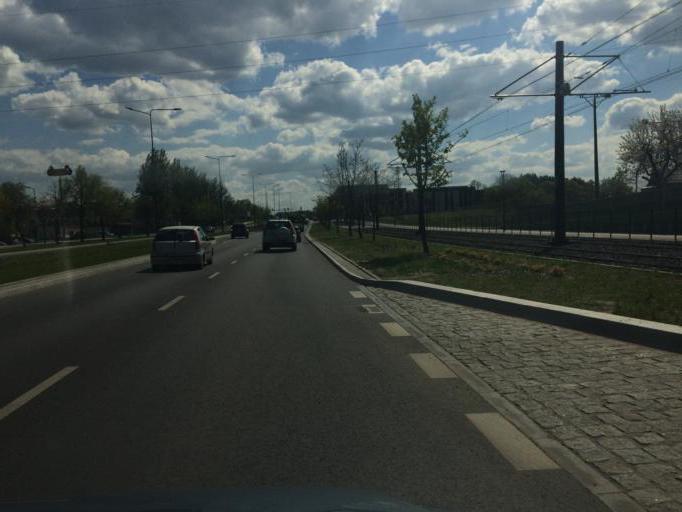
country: PL
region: Warmian-Masurian Voivodeship
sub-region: Powiat olsztynski
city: Olsztyn
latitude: 53.7588
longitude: 20.4866
